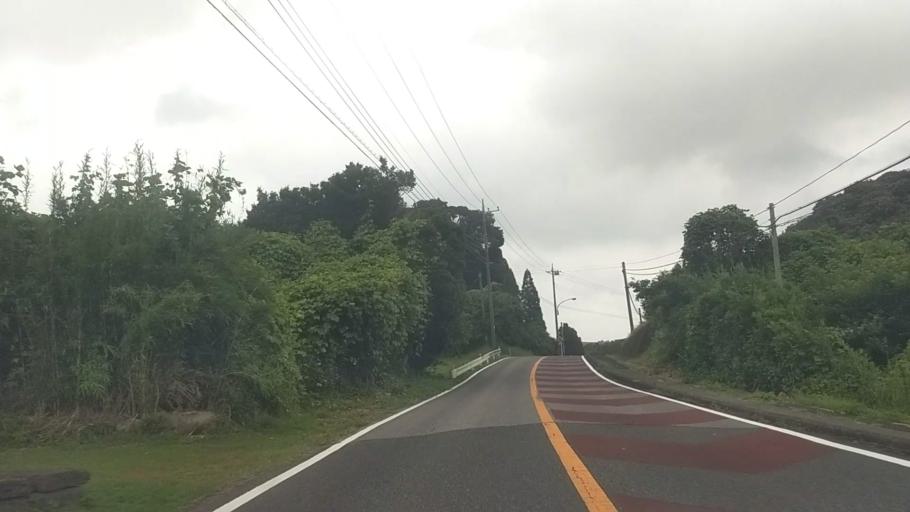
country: JP
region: Chiba
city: Katsuura
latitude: 35.2496
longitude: 140.2133
